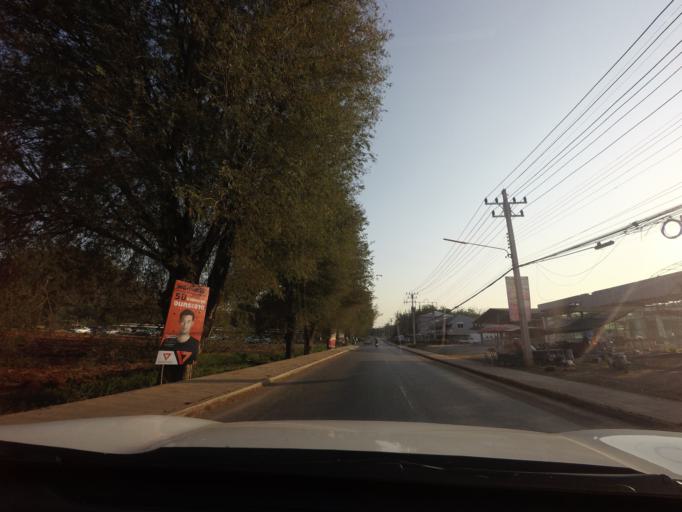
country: TH
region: Nakhon Ratchasima
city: Pak Chong
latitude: 14.6479
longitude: 101.3562
